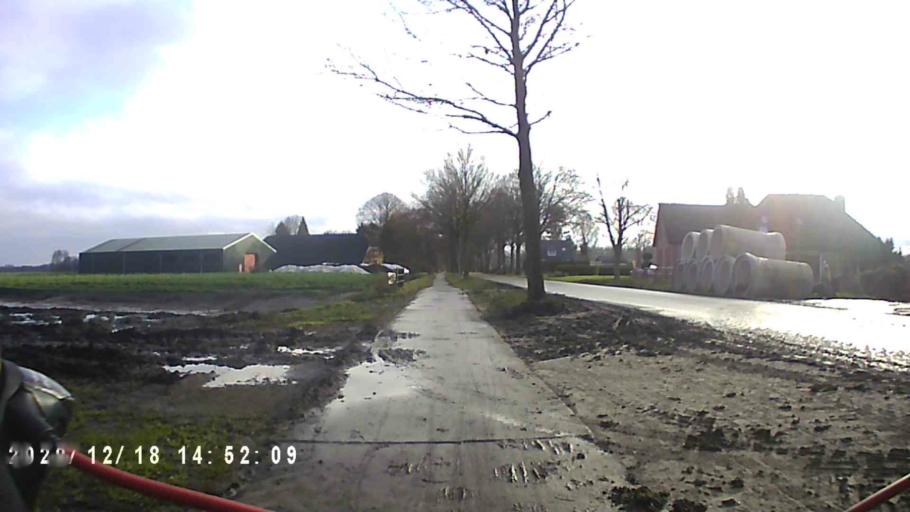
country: NL
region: Groningen
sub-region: Gemeente Haren
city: Haren
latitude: 53.1934
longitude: 6.6766
